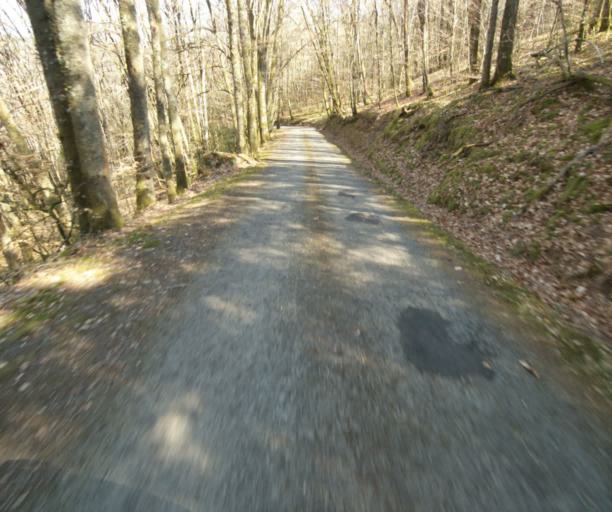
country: FR
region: Limousin
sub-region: Departement de la Correze
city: Chamboulive
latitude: 45.4882
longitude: 1.7444
